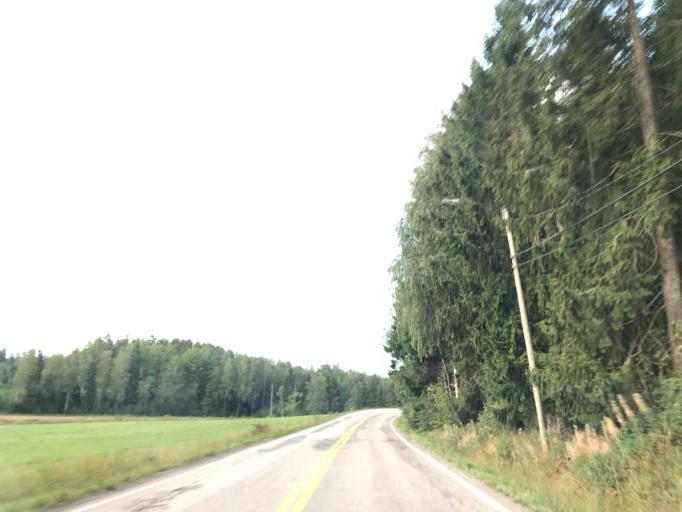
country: FI
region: Uusimaa
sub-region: Helsinki
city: Vihti
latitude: 60.3819
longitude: 24.5250
